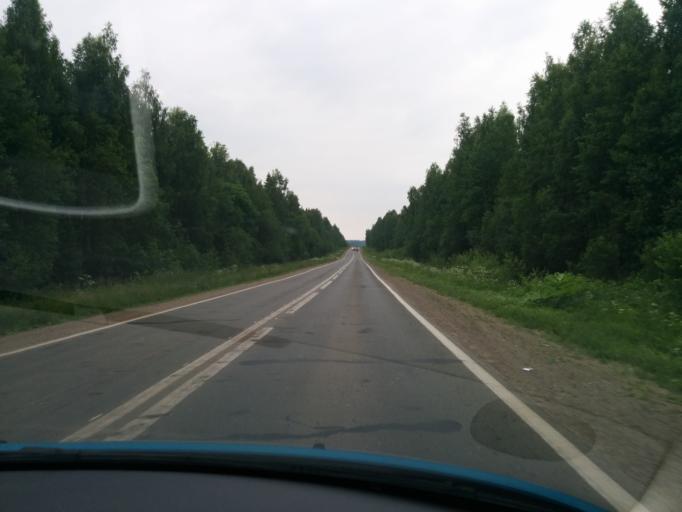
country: RU
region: Perm
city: Perm
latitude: 58.1476
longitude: 56.2605
